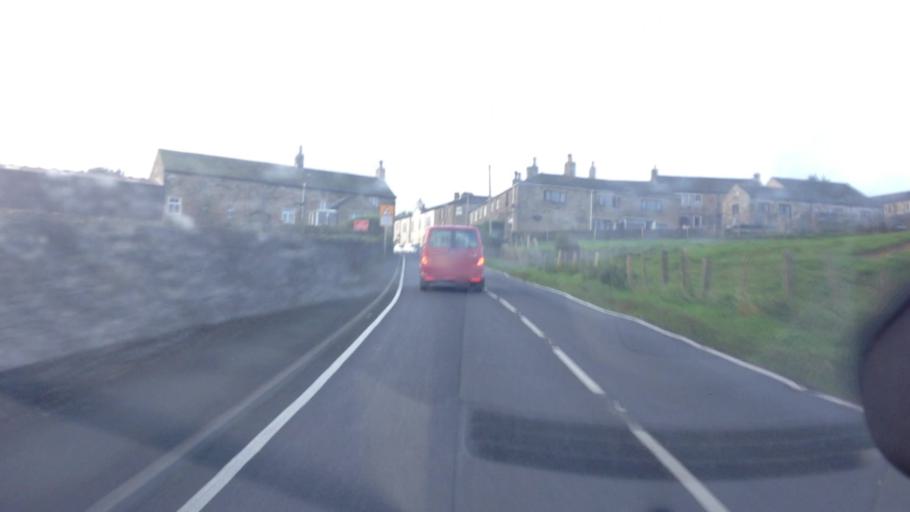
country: GB
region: England
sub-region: Kirklees
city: Mirfield
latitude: 53.6692
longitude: -1.7325
